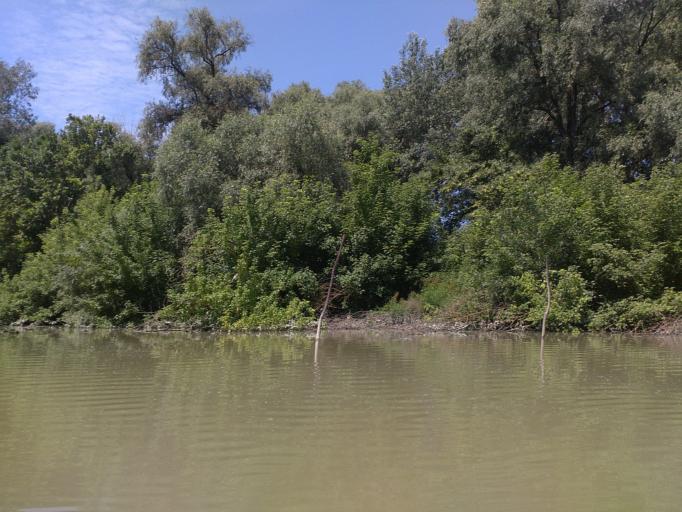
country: SK
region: Nitriansky
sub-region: Okres Nove Zamky
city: Sturovo
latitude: 47.7630
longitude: 18.6878
